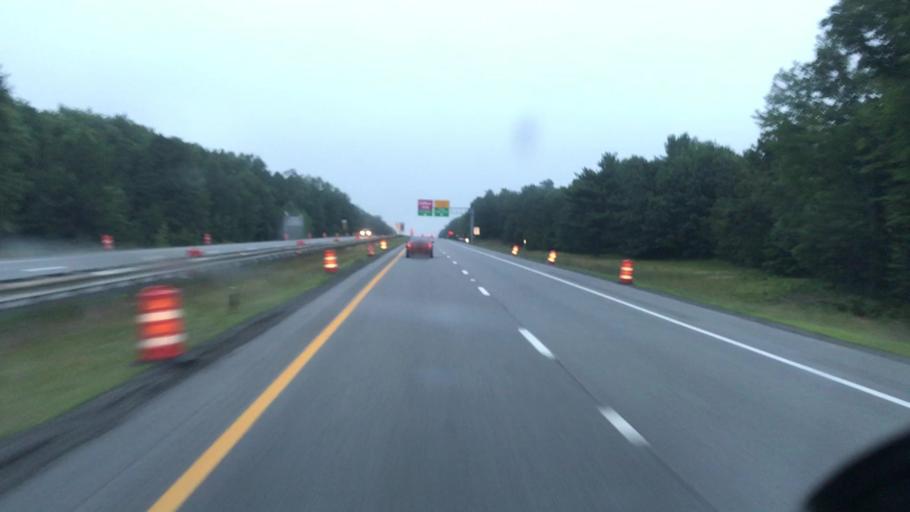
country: US
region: Maine
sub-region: Cumberland County
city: New Gloucester
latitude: 43.9244
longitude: -70.3370
